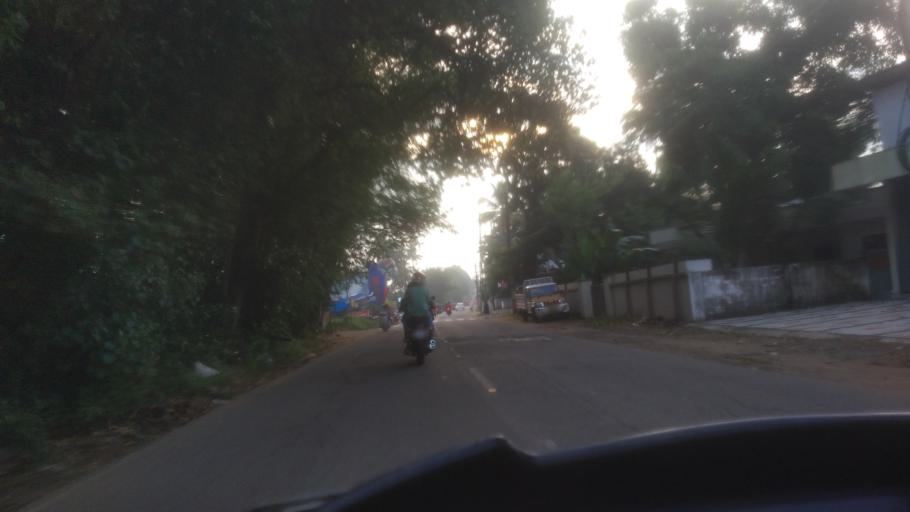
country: IN
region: Kerala
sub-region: Ernakulam
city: Perumpavur
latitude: 10.1199
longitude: 76.4379
